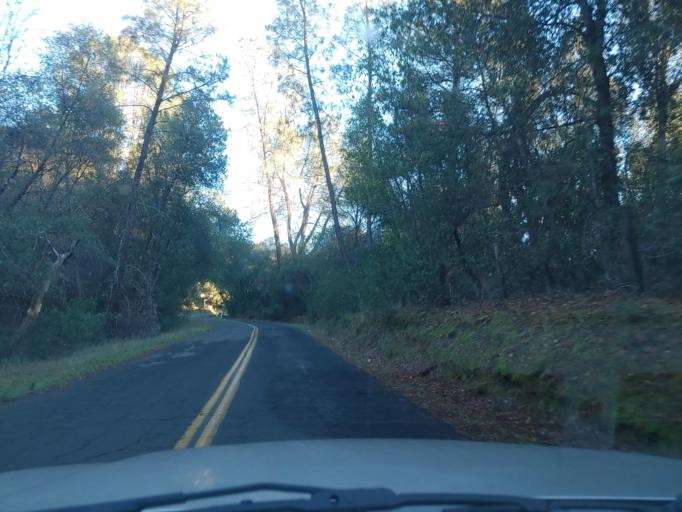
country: US
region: California
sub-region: Tuolumne County
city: Columbia
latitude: 38.0373
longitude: -120.3738
